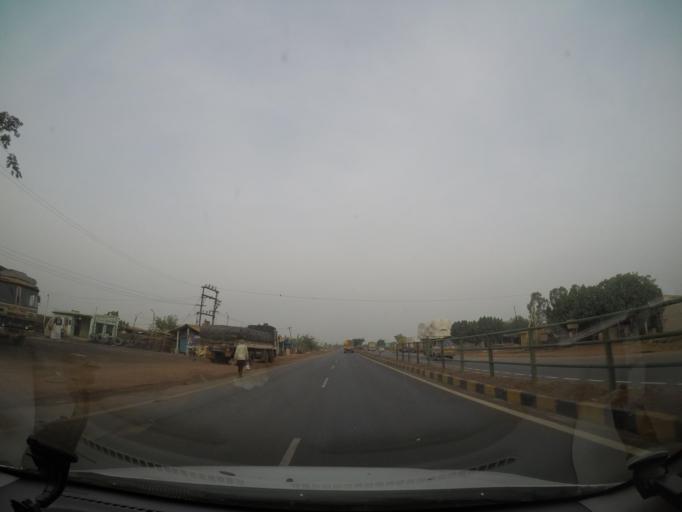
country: IN
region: Andhra Pradesh
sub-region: West Godavari
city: Eluru
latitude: 16.6324
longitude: 80.9555
